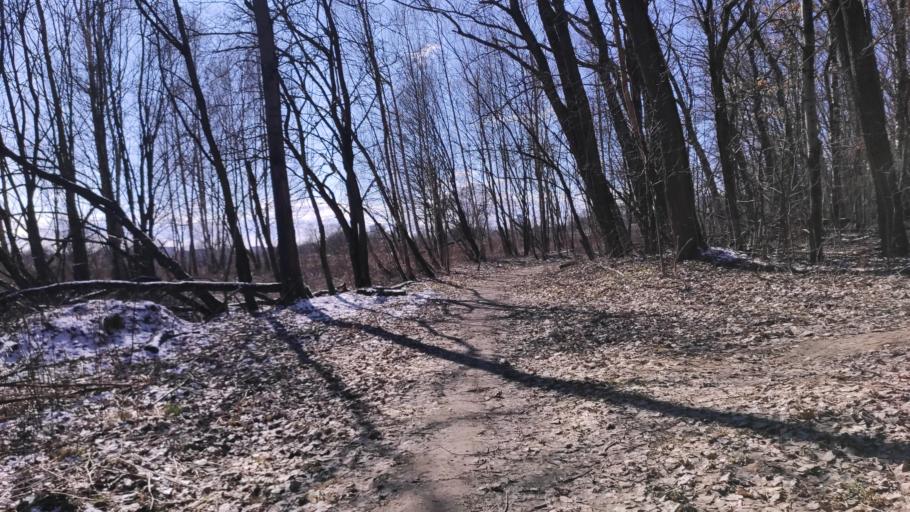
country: BY
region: Minsk
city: Novoye Medvezhino
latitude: 53.8870
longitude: 27.4725
